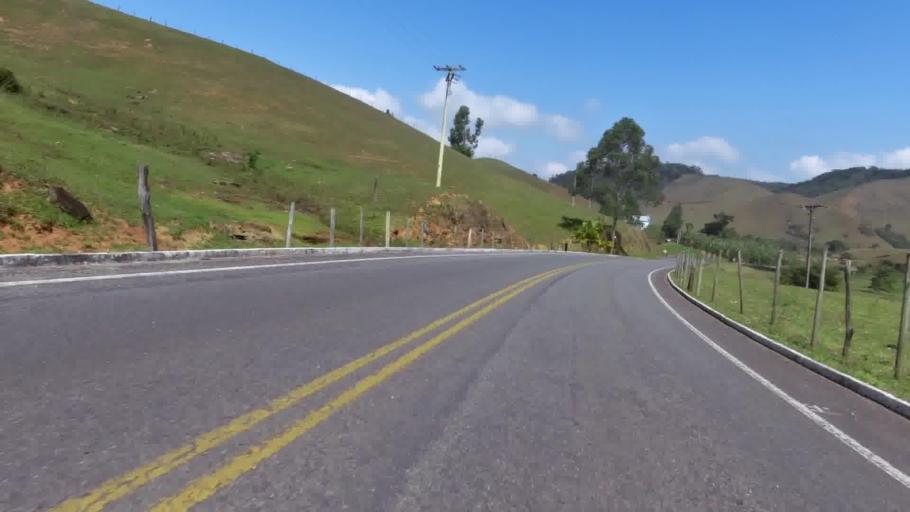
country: BR
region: Espirito Santo
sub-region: Alfredo Chaves
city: Alfredo Chaves
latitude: -20.5667
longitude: -40.8067
